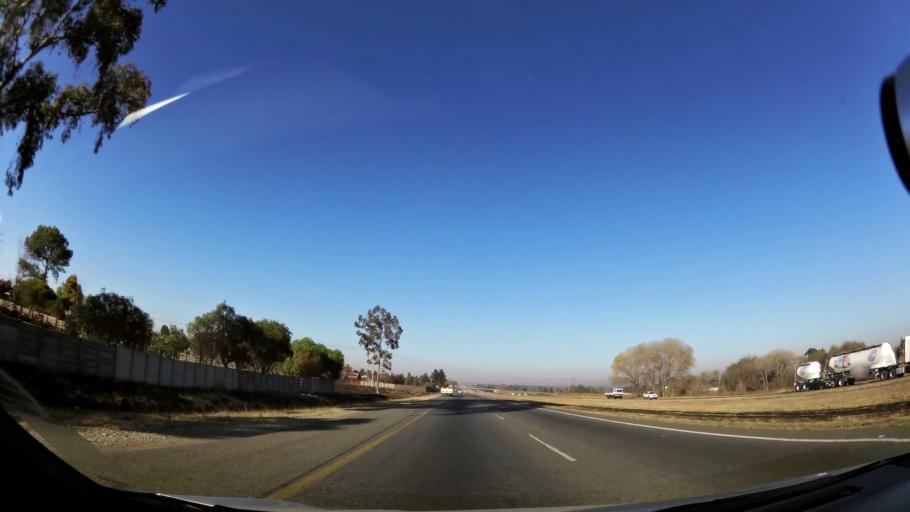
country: ZA
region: Gauteng
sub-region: Ekurhuleni Metropolitan Municipality
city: Germiston
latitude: -26.3327
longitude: 28.1100
